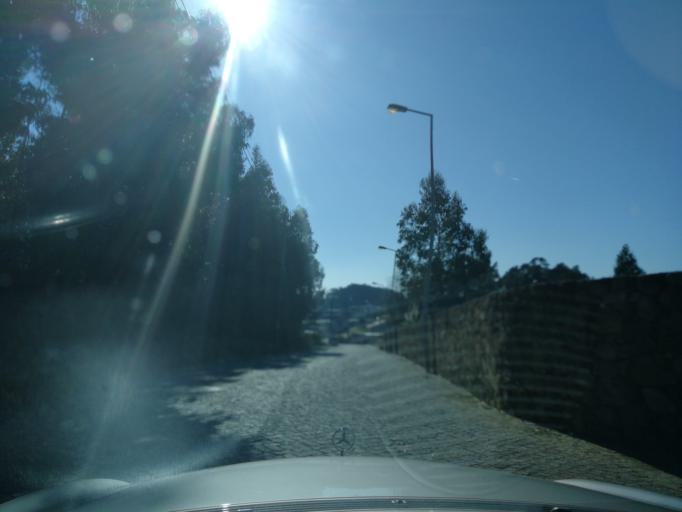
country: PT
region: Porto
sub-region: Vila do Conde
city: Vila do Conde
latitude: 41.3721
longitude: -8.7326
